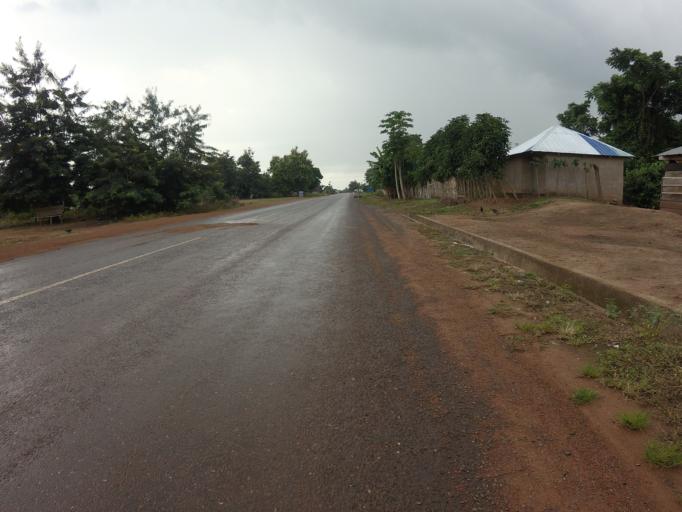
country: GH
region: Volta
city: Hohoe
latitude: 7.0396
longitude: 0.4268
